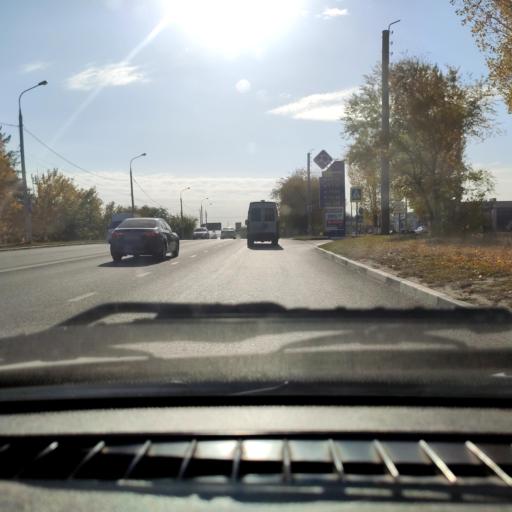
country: RU
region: Samara
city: Zhigulevsk
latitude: 53.4997
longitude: 49.4724
